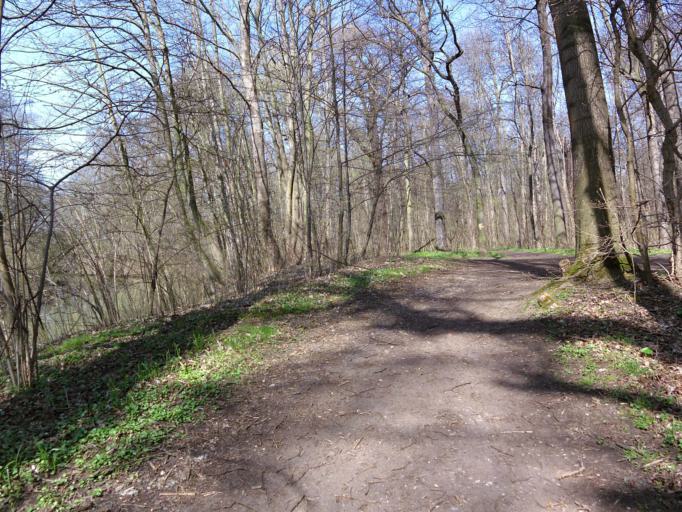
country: DE
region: Saxony
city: Leipzig
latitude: 51.3527
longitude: 12.3471
